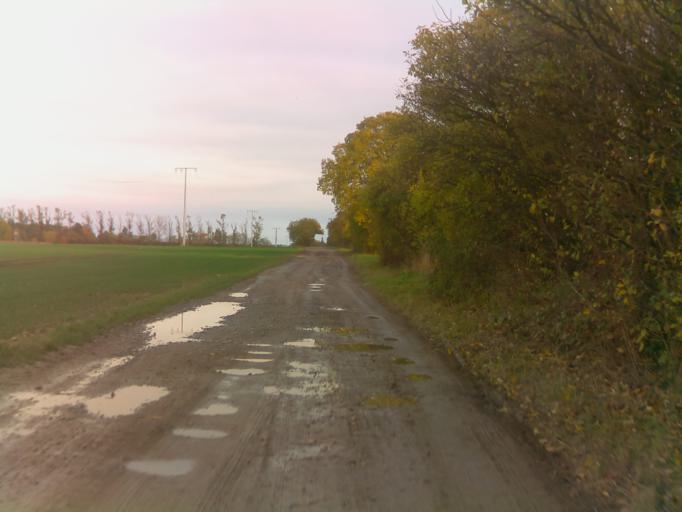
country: DE
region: Thuringia
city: Blankenhain
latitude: 50.8409
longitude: 11.3852
